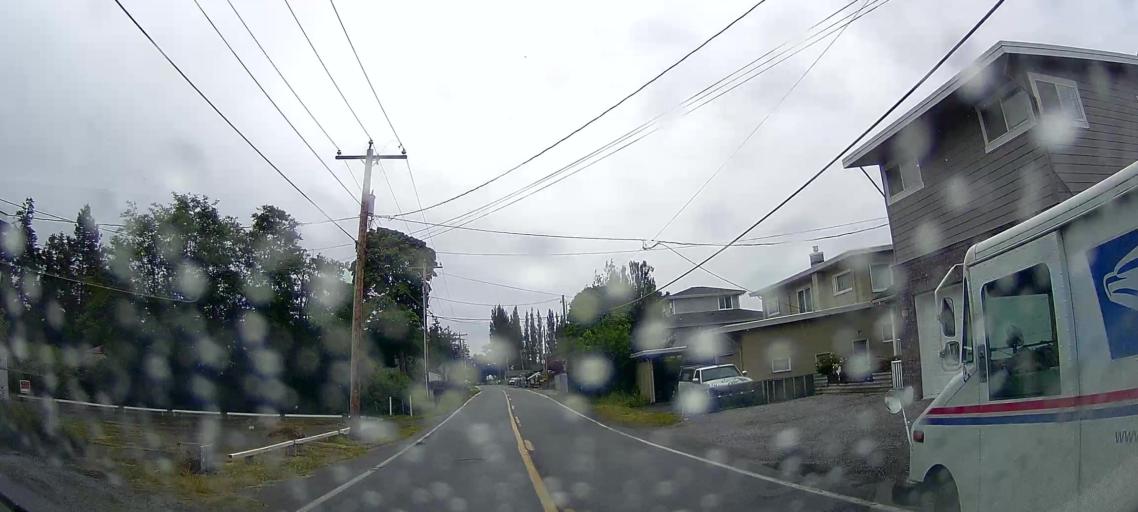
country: US
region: Washington
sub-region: Whatcom County
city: Birch Bay
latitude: 48.8153
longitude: -122.7086
